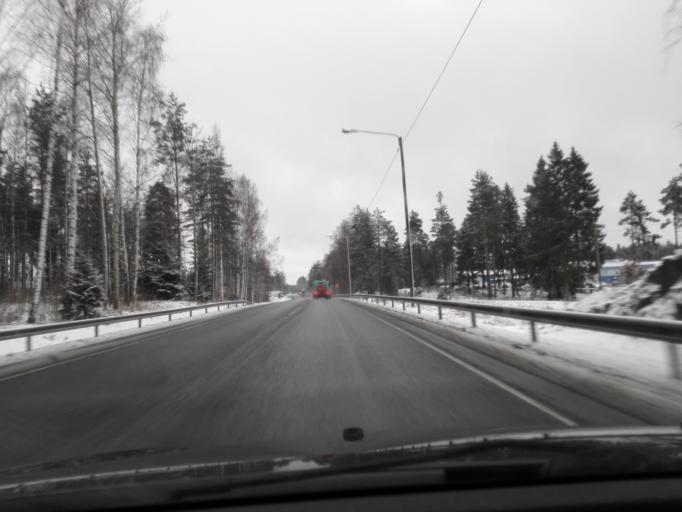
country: FI
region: Uusimaa
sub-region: Helsinki
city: Vantaa
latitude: 60.2998
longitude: 25.1033
